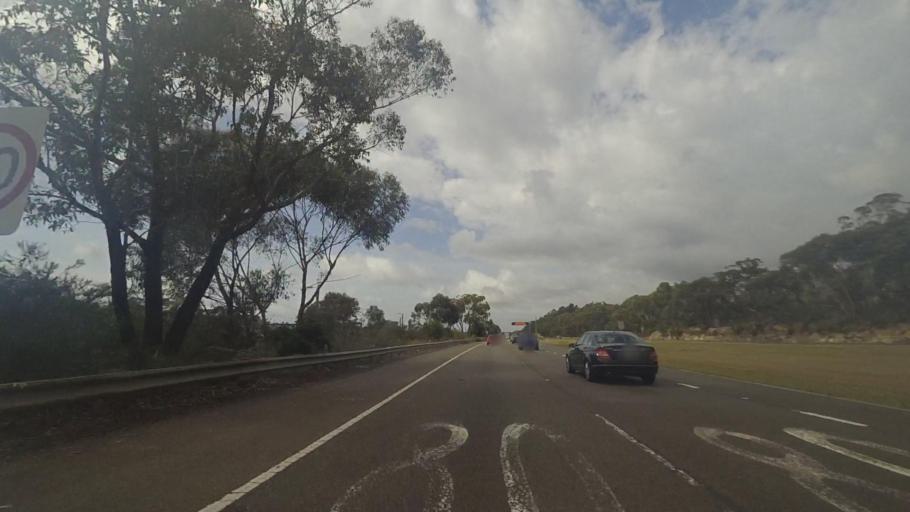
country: AU
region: New South Wales
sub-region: Sutherland Shire
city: Heathcote
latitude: -34.1258
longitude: 150.9931
